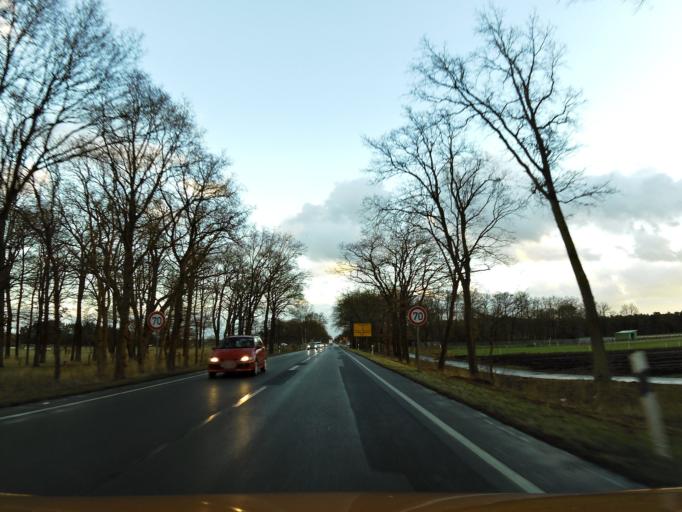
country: DE
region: Lower Saxony
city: Broeckel
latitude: 52.4810
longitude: 10.2613
